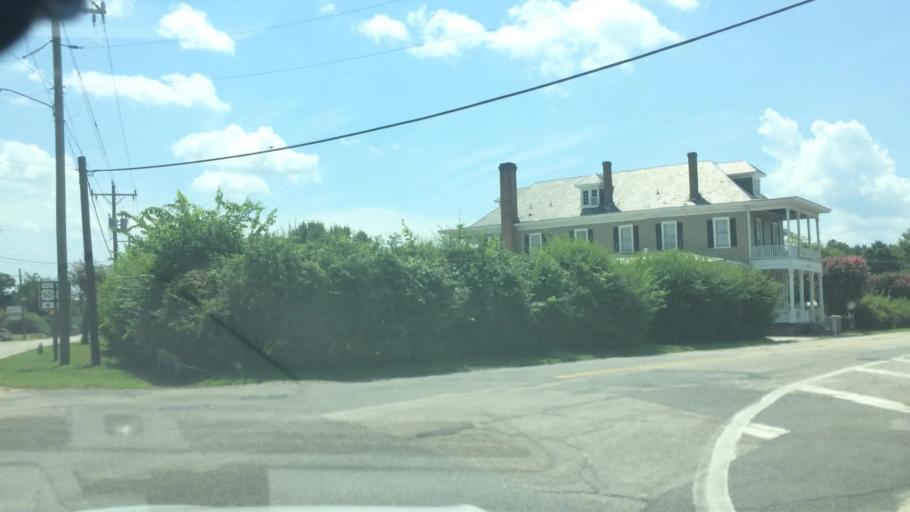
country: US
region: Virginia
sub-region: York County
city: Yorktown
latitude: 37.1944
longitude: -76.5716
